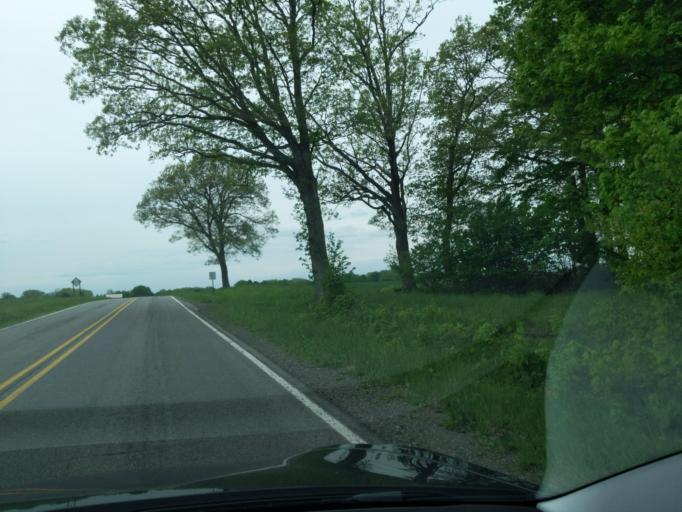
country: US
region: Michigan
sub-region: Ingham County
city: Leslie
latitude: 42.4475
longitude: -84.3661
